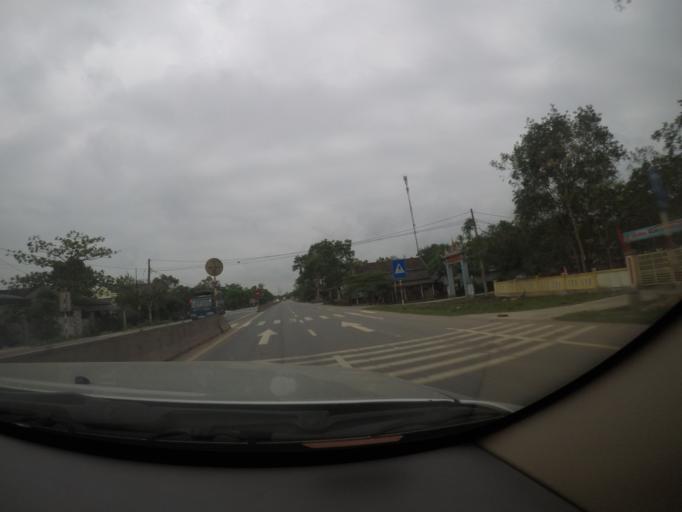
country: VN
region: Thua Thien-Hue
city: Phong Dien
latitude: 16.6062
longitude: 107.3234
